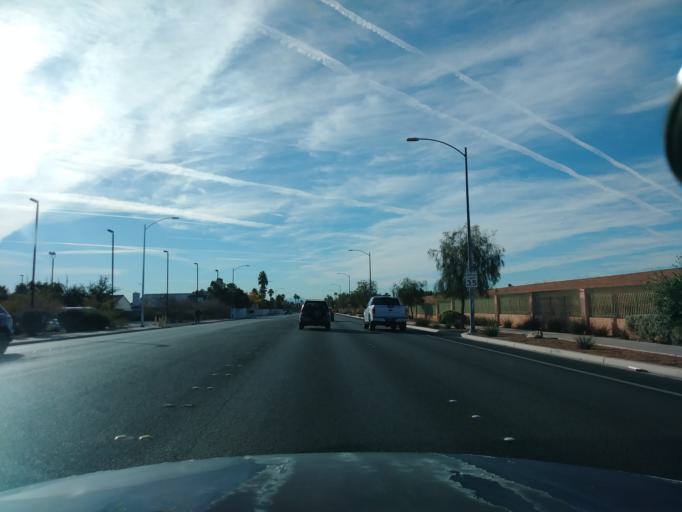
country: US
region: Nevada
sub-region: Clark County
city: Spring Valley
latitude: 36.1512
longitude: -115.2344
